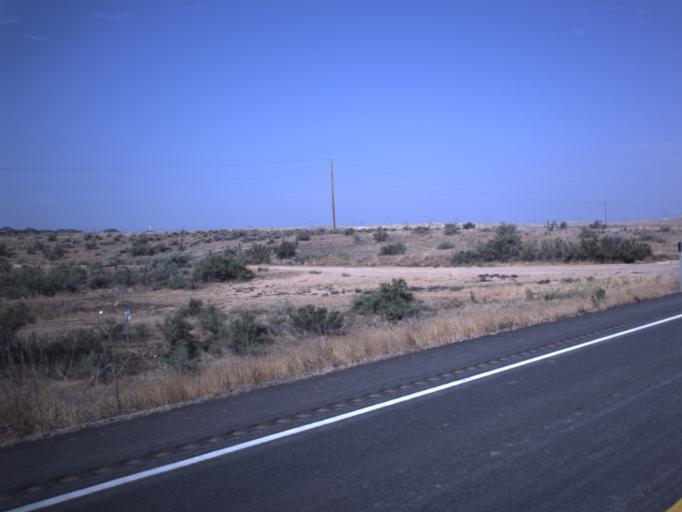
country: US
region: Utah
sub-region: Uintah County
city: Naples
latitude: 40.3086
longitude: -109.2167
